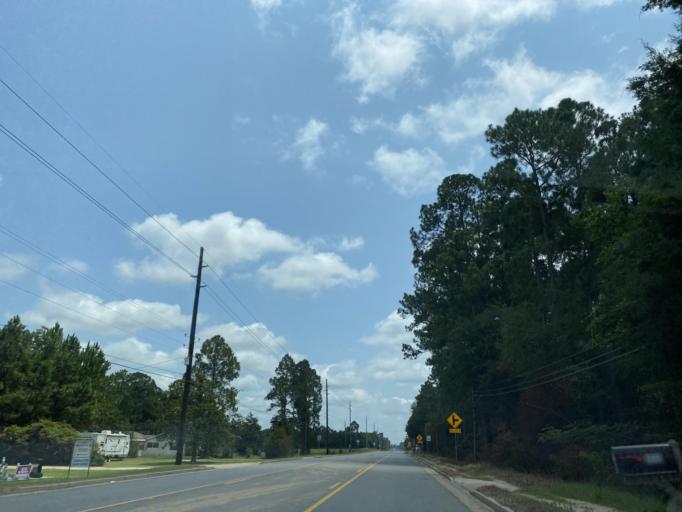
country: US
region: Georgia
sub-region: Jeff Davis County
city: Hazlehurst
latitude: 31.8418
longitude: -82.5841
